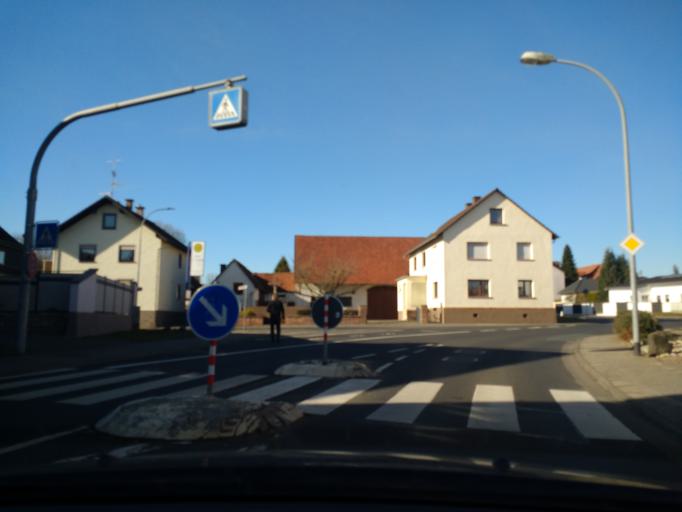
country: DE
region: Bavaria
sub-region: Regierungsbezirk Unterfranken
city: Geiselbach
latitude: 50.1445
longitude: 9.1414
